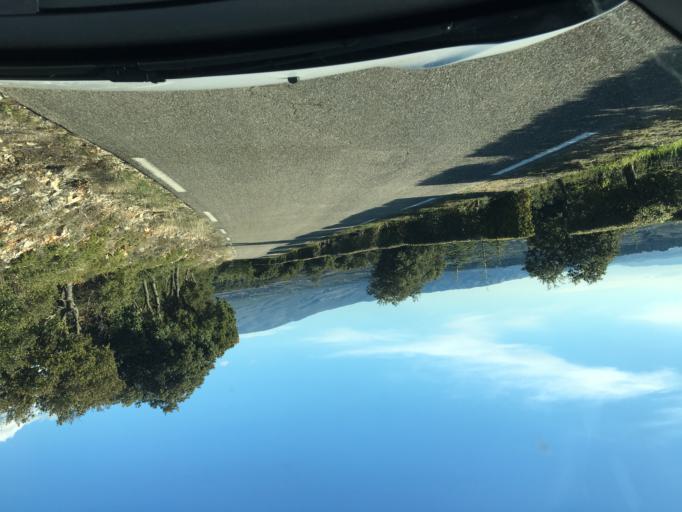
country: FR
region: Provence-Alpes-Cote d'Azur
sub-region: Departement du Vaucluse
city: Villes-sur-Auzon
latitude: 44.0476
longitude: 5.2461
